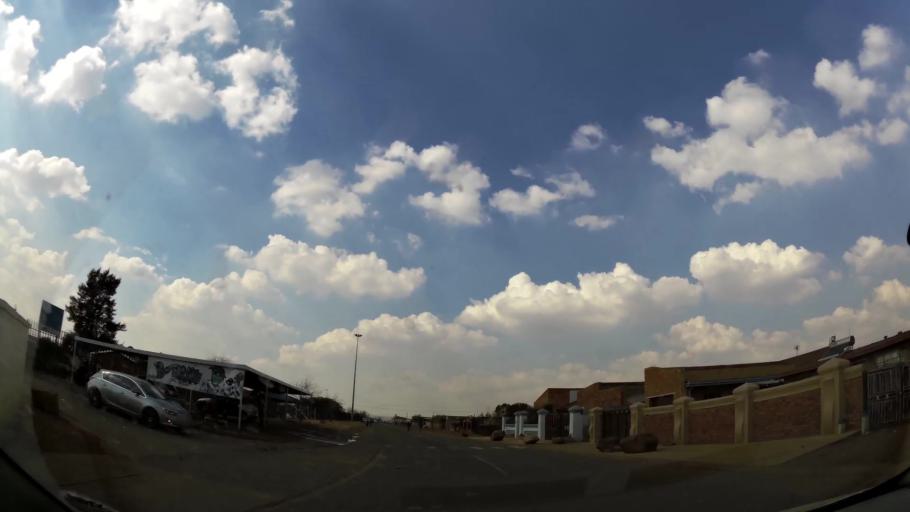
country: ZA
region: Gauteng
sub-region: Ekurhuleni Metropolitan Municipality
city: Germiston
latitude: -26.3522
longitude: 28.1414
